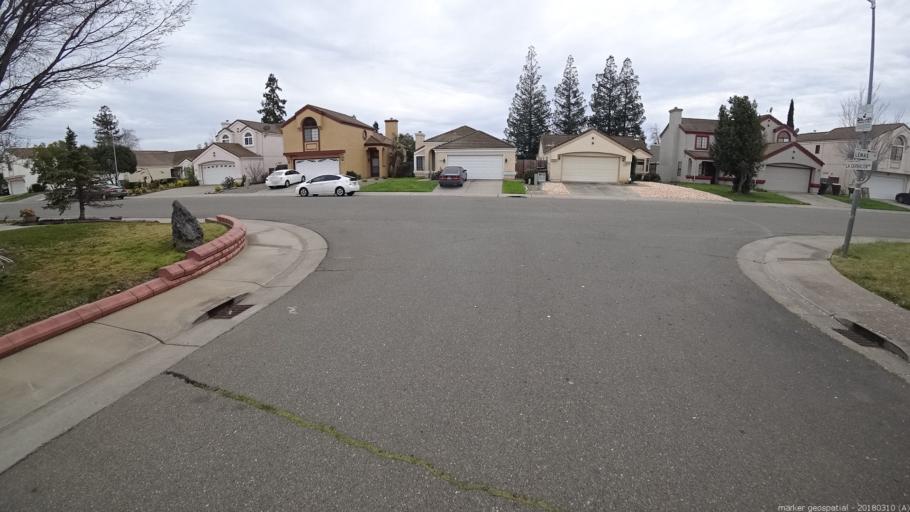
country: US
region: California
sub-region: Sacramento County
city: Vineyard
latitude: 38.4676
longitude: -121.3748
